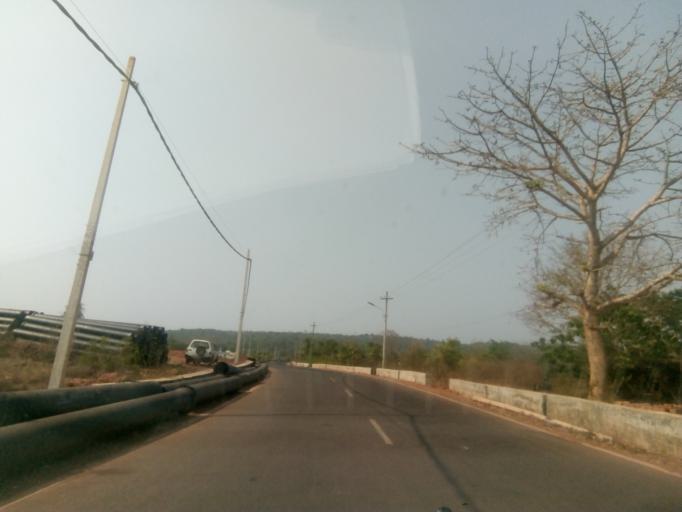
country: IN
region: Goa
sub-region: North Goa
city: Pernem
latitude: 15.7108
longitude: 73.8542
